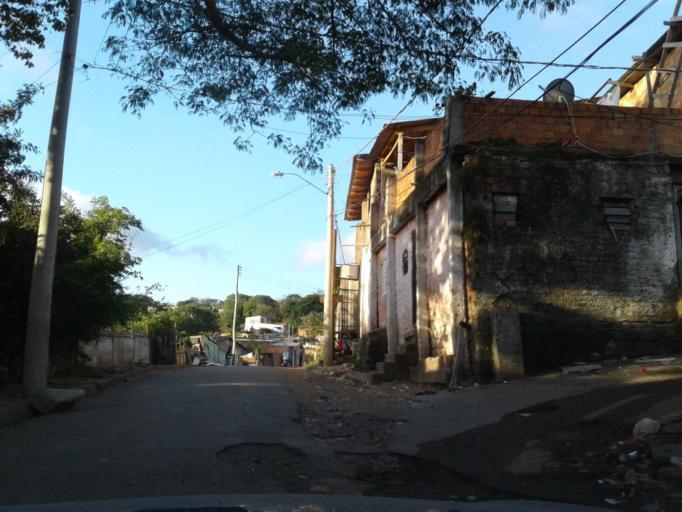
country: BR
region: Rio Grande do Sul
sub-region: Porto Alegre
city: Porto Alegre
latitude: -30.0488
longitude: -51.1533
